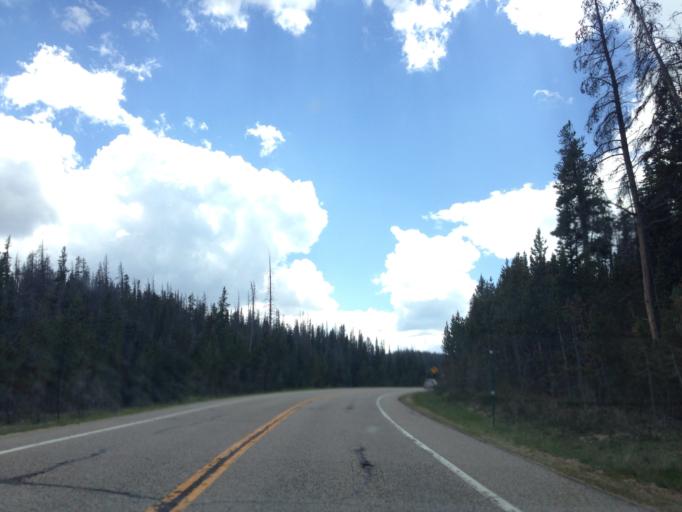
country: US
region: Colorado
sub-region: Larimer County
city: Estes Park
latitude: 40.5767
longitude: -105.8584
